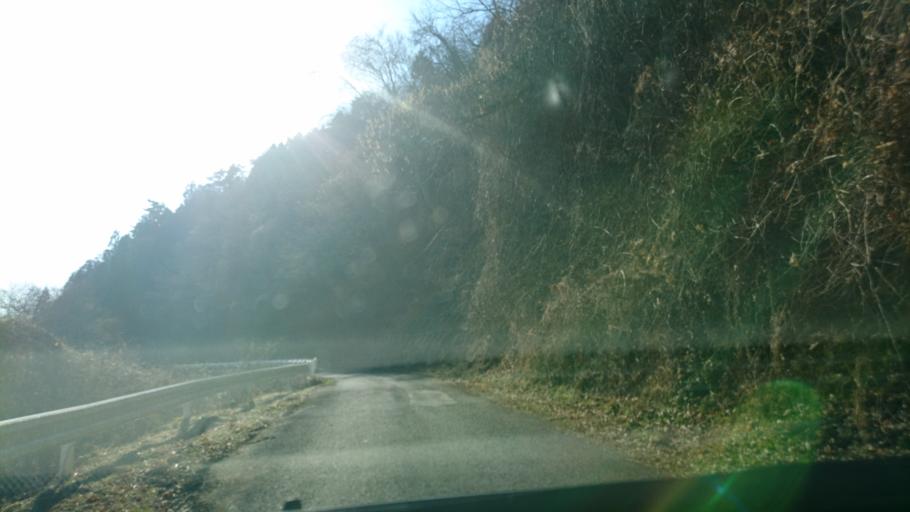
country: JP
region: Iwate
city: Ichinoseki
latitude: 38.8011
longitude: 141.2611
